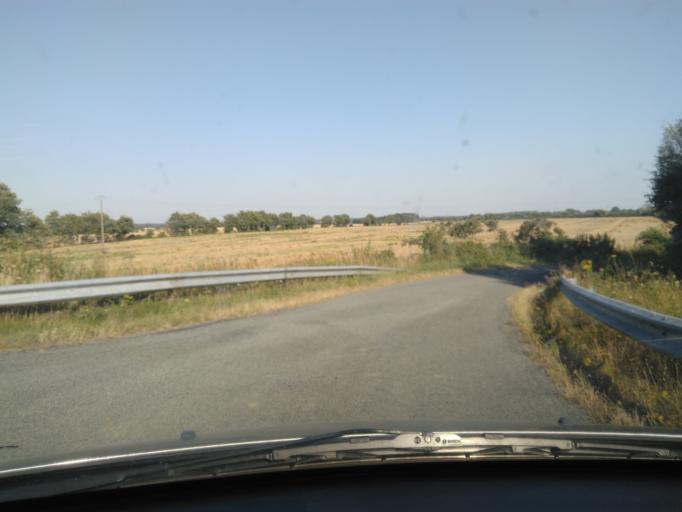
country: FR
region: Pays de la Loire
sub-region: Departement de la Vendee
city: Les Essarts
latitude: 46.7634
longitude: -1.2692
